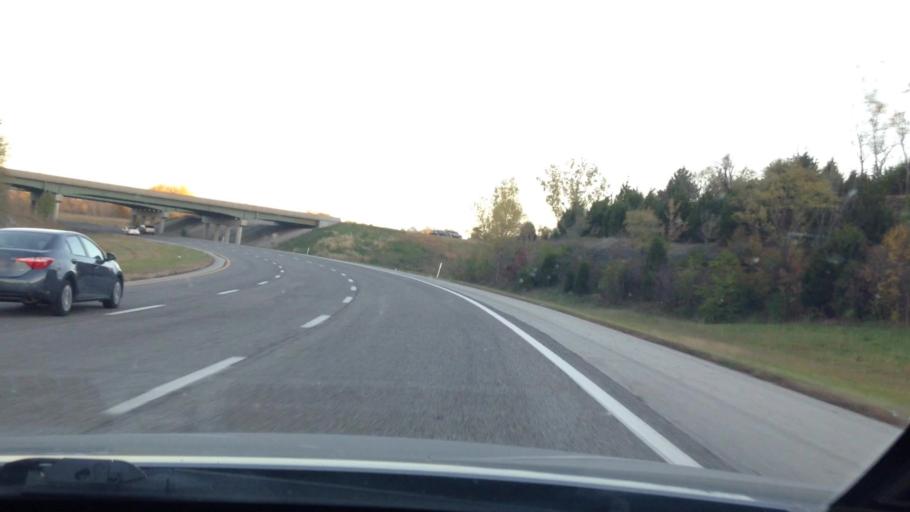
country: US
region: Kansas
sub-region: Wyandotte County
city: Edwardsville
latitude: 39.1045
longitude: -94.8134
